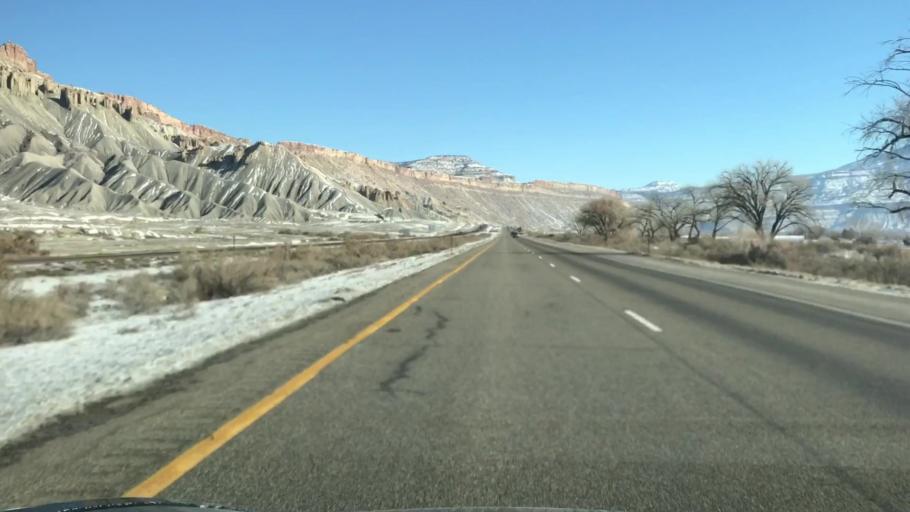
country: US
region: Colorado
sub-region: Mesa County
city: Clifton
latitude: 39.1095
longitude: -108.4219
